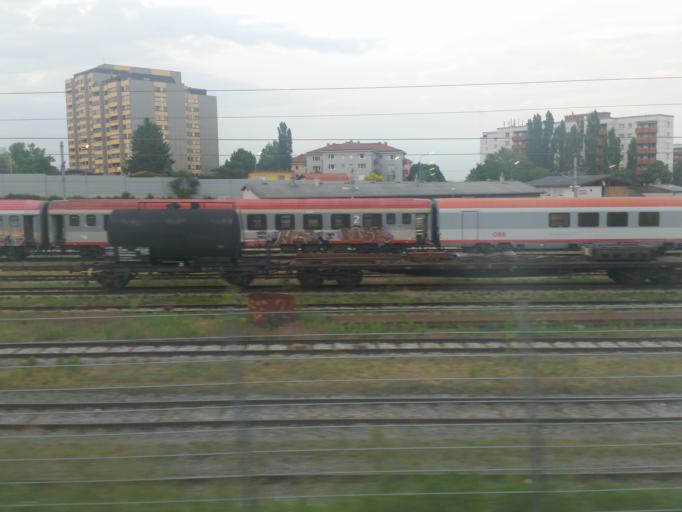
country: AT
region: Vienna
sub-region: Wien Stadt
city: Vienna
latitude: 48.1719
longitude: 16.4011
